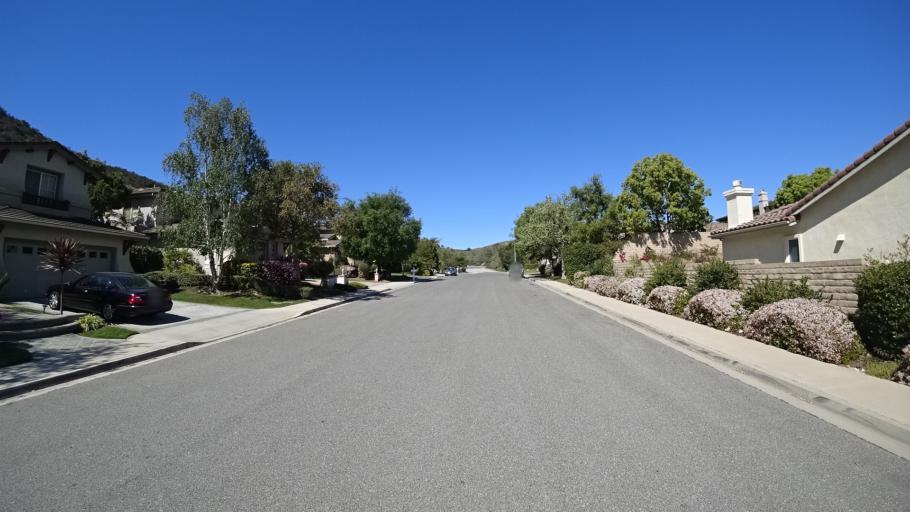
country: US
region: California
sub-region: Ventura County
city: Casa Conejo
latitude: 34.1649
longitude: -118.9761
